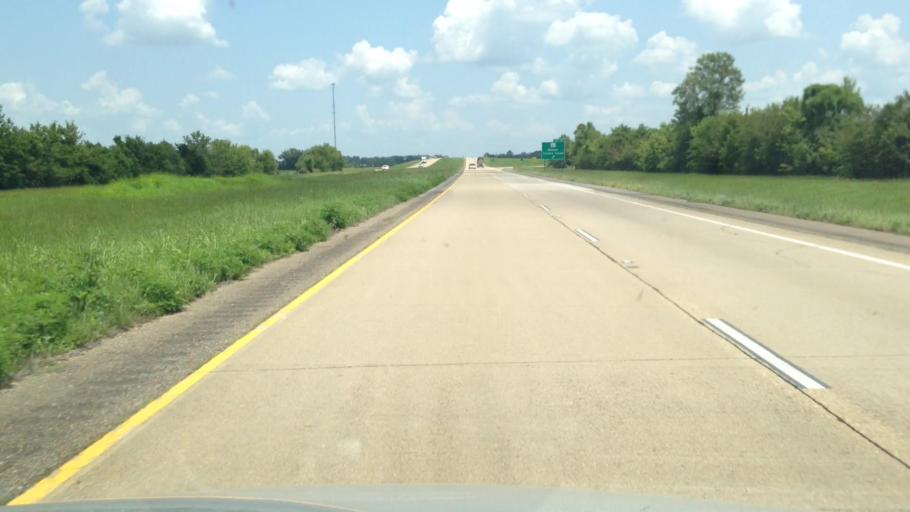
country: US
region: Louisiana
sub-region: Rapides Parish
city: Lecompte
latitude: 31.0176
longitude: -92.3839
